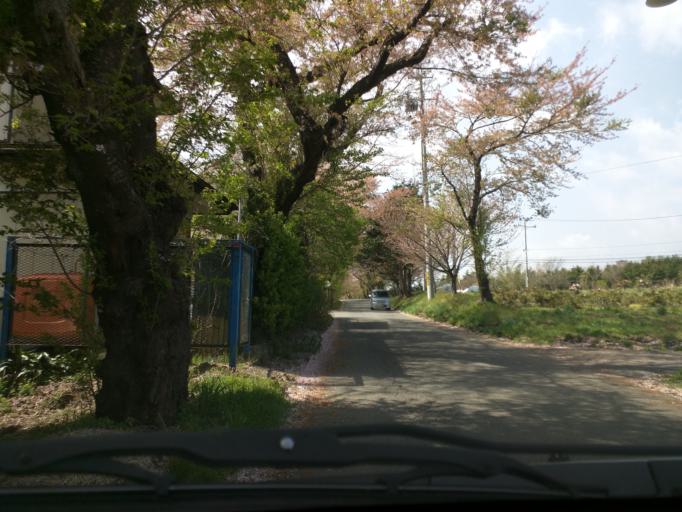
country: JP
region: Fukushima
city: Nihommatsu
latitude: 37.6030
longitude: 140.3594
